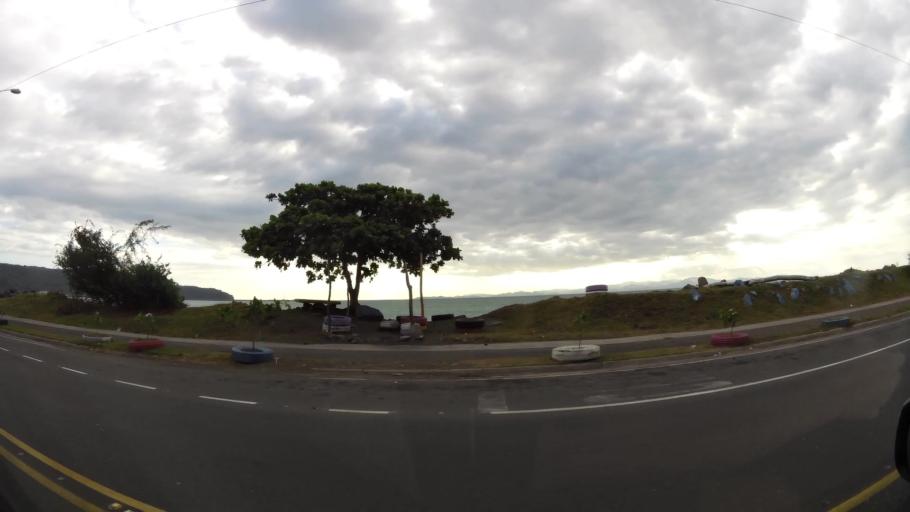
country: CR
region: Puntarenas
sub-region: Canton Central de Puntarenas
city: Chacarita
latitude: 9.9298
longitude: -84.7181
